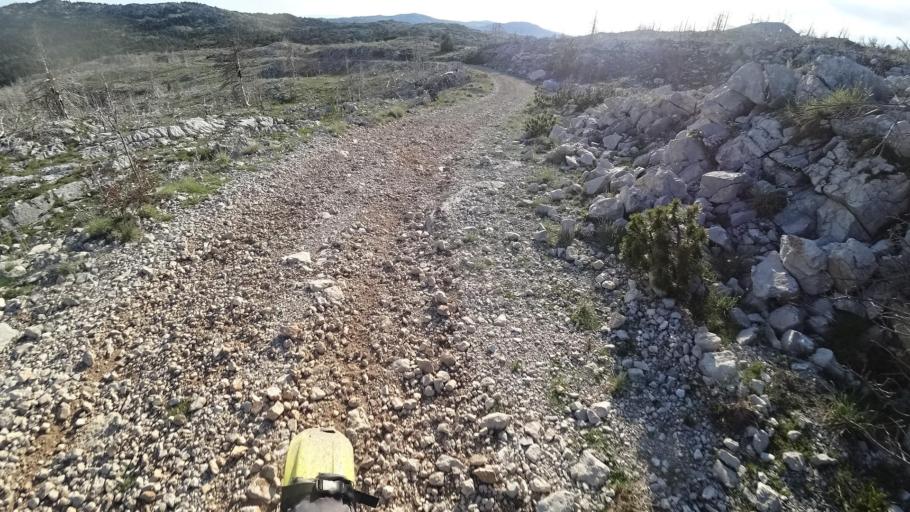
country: BA
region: Federation of Bosnia and Herzegovina
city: Kocerin
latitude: 43.5751
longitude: 17.5391
